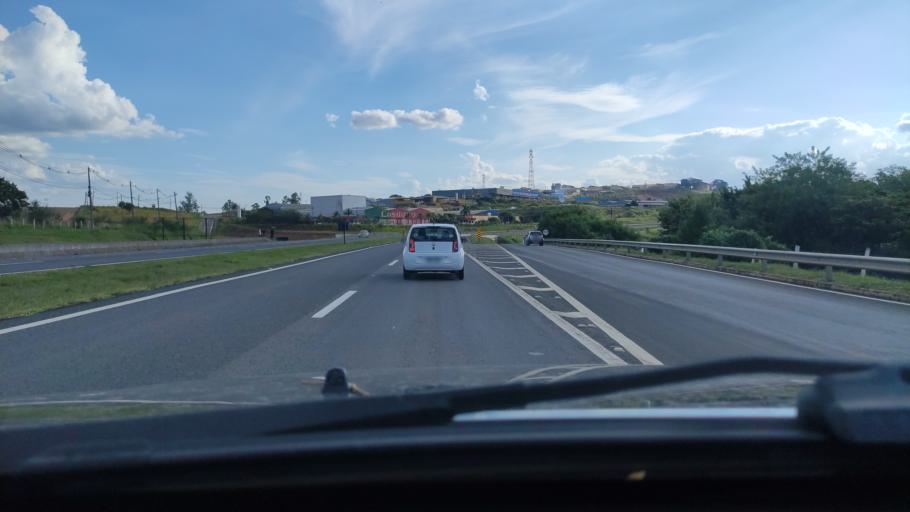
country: BR
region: Sao Paulo
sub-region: Itapira
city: Itapira
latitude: -22.4504
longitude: -46.8389
